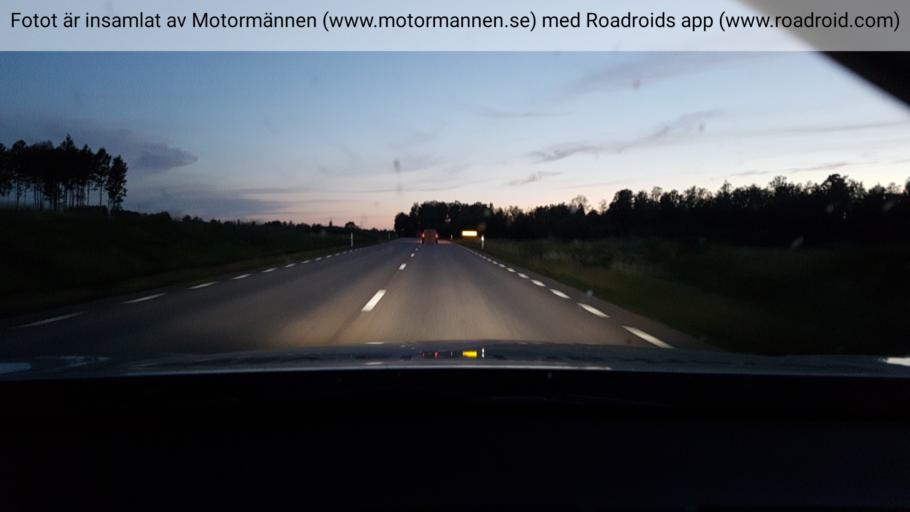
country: SE
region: Vaestra Goetaland
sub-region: Tibro Kommun
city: Tibro
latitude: 58.4557
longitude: 14.2383
